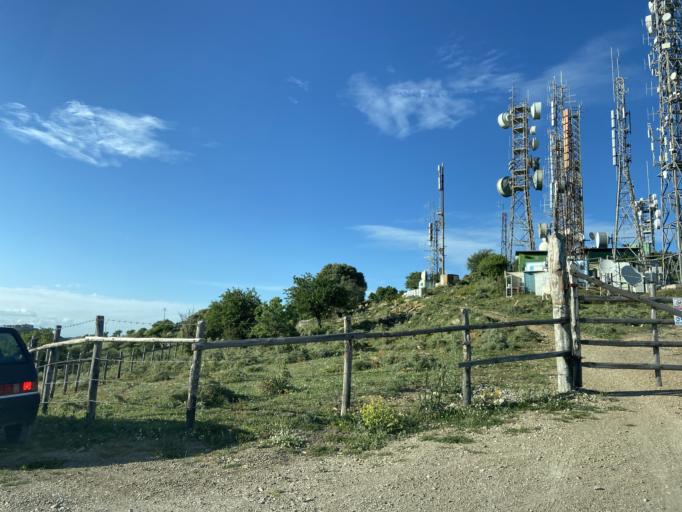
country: IT
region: Latium
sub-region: Citta metropolitana di Roma Capitale
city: Santa Marinella
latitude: 42.0893
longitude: 11.8526
